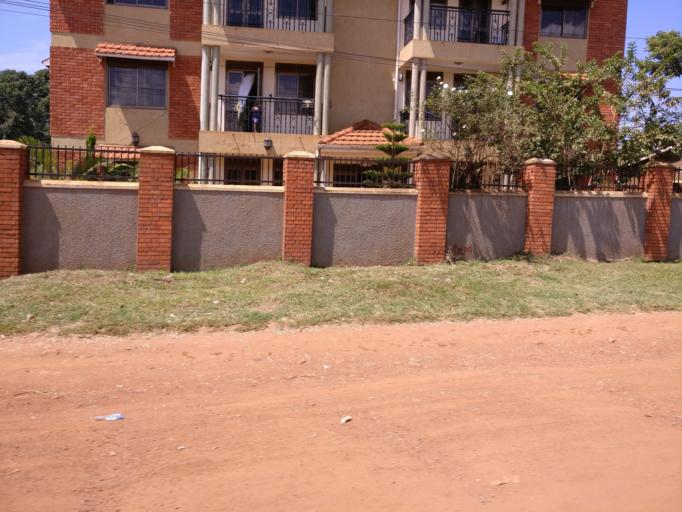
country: UG
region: Central Region
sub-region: Wakiso District
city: Entebbe
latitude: 0.1021
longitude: 32.5092
